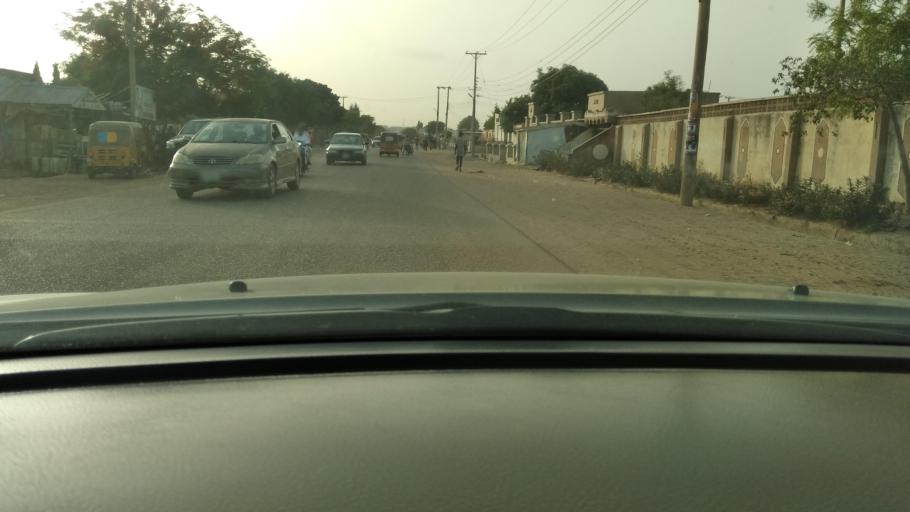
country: NG
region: Kano
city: Kano
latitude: 11.9541
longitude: 8.5233
